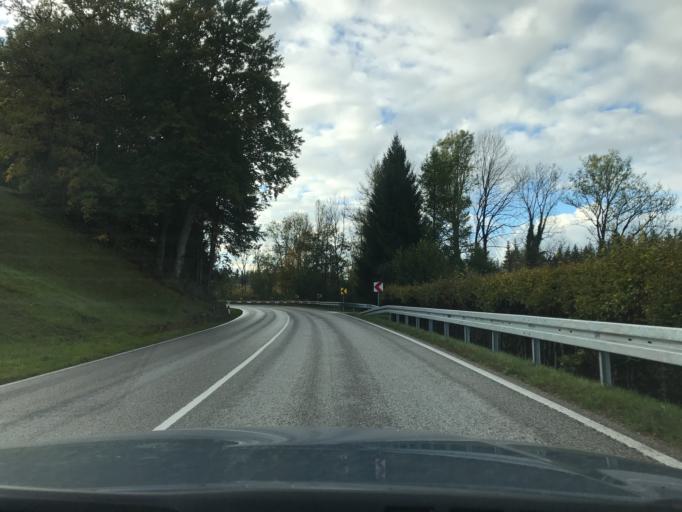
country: DE
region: Bavaria
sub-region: Upper Bavaria
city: Konigsdorf
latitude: 47.8271
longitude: 11.5331
